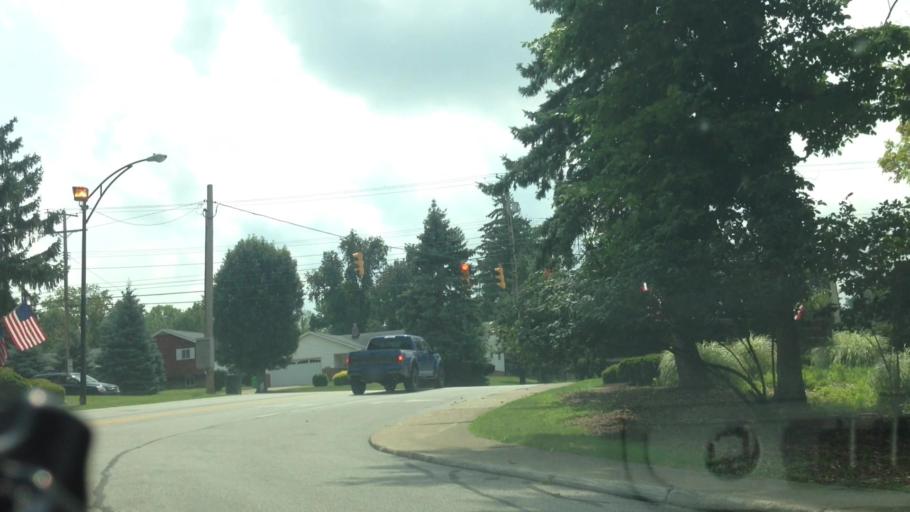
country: US
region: Ohio
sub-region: Cuyahoga County
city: Highland Heights
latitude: 41.5394
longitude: -81.4667
